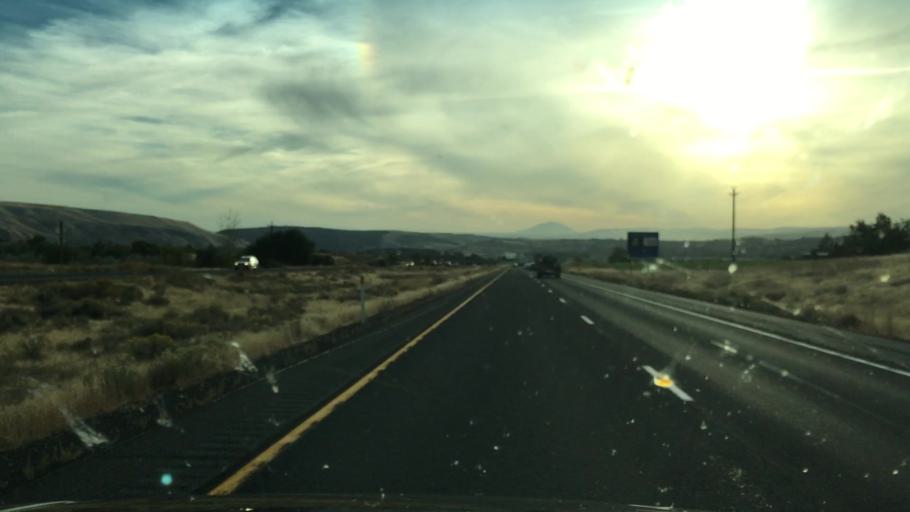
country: US
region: Washington
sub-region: Yakima County
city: Selah
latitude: 46.6840
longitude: -120.4702
